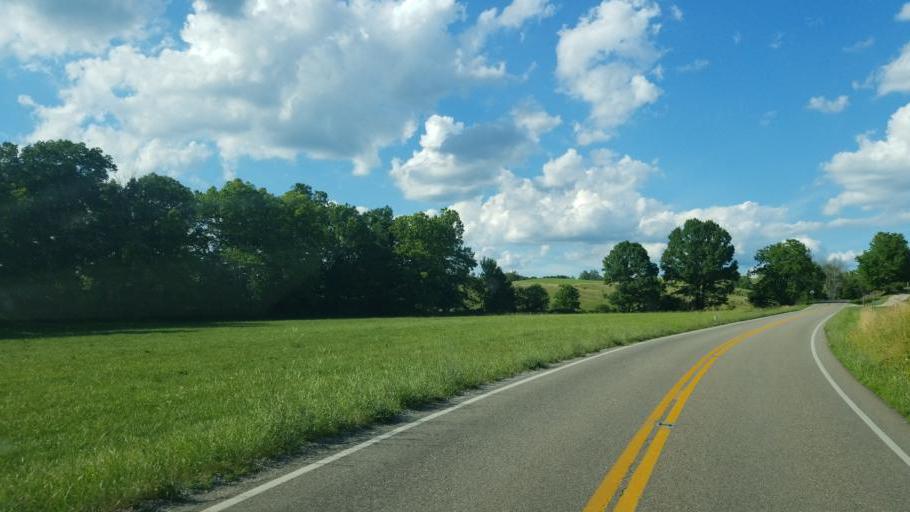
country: US
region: Ohio
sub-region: Gallia County
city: Gallipolis
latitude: 38.8009
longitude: -82.3256
